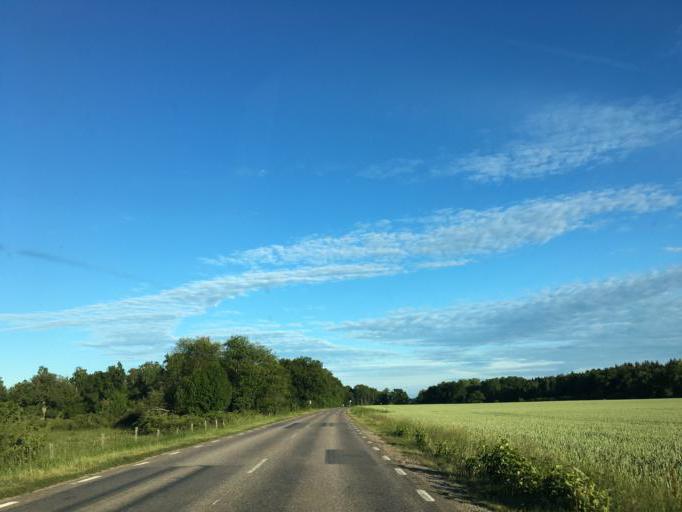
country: SE
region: Vaestmanland
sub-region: Vasteras
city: Vasteras
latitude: 59.5551
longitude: 16.5327
